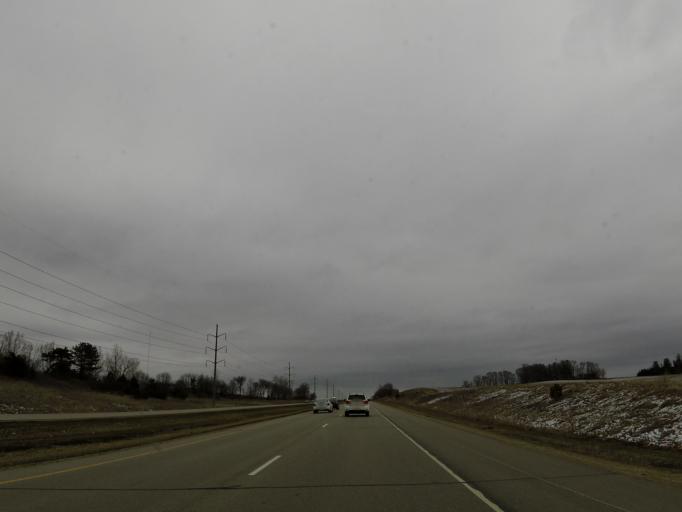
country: US
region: Minnesota
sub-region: Olmsted County
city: Byron
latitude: 44.0289
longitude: -92.6164
